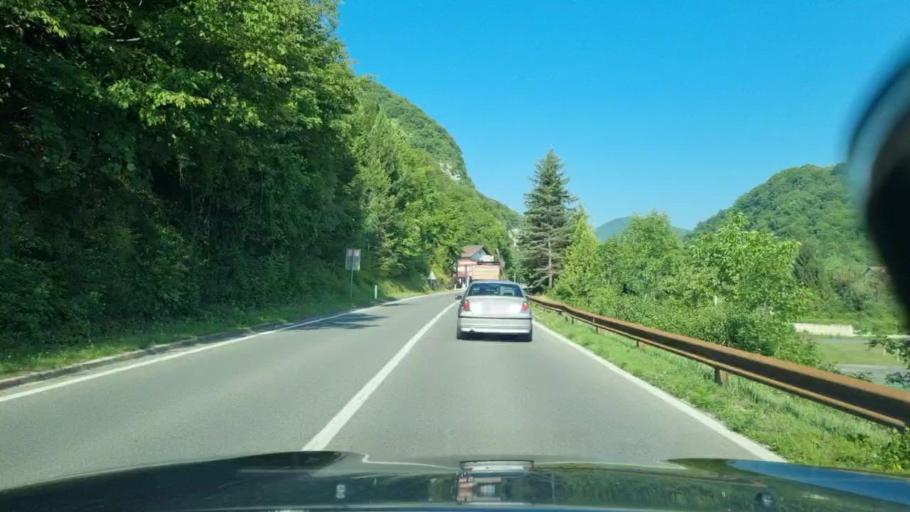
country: BA
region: Federation of Bosnia and Herzegovina
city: Jajce
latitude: 44.3443
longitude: 17.2520
